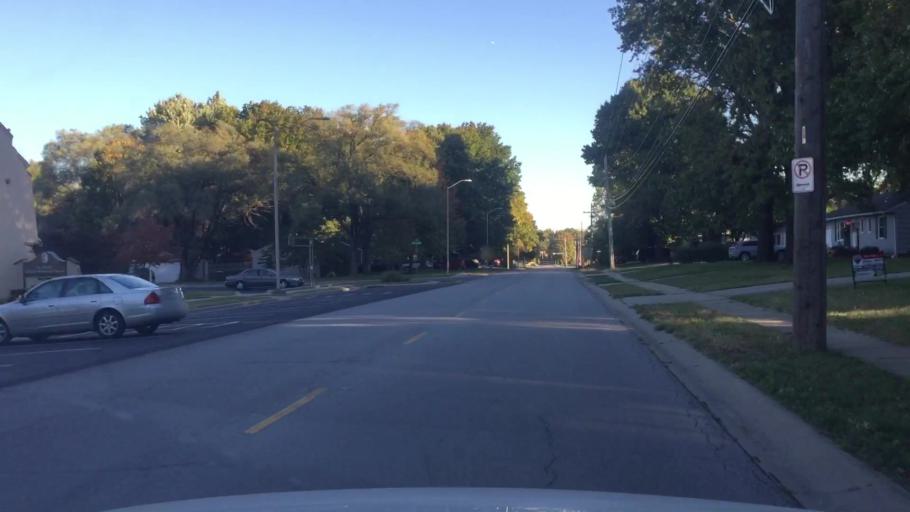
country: US
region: Kansas
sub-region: Johnson County
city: Mission
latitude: 39.0116
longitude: -94.6722
